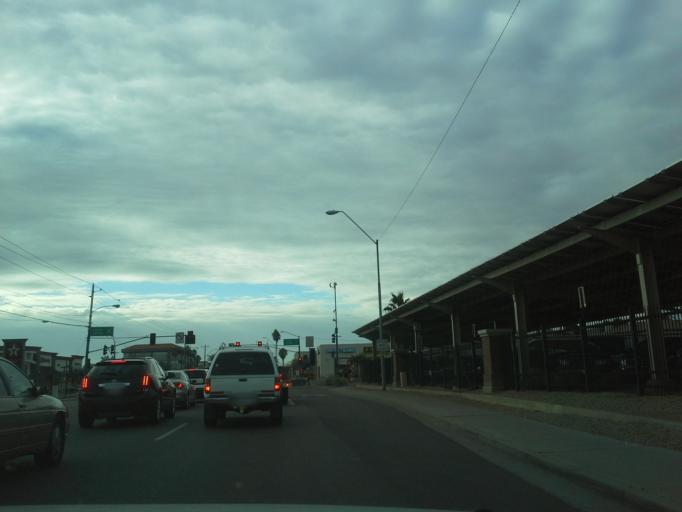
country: US
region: Arizona
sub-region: Maricopa County
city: Phoenix
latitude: 33.4956
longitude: -112.0651
